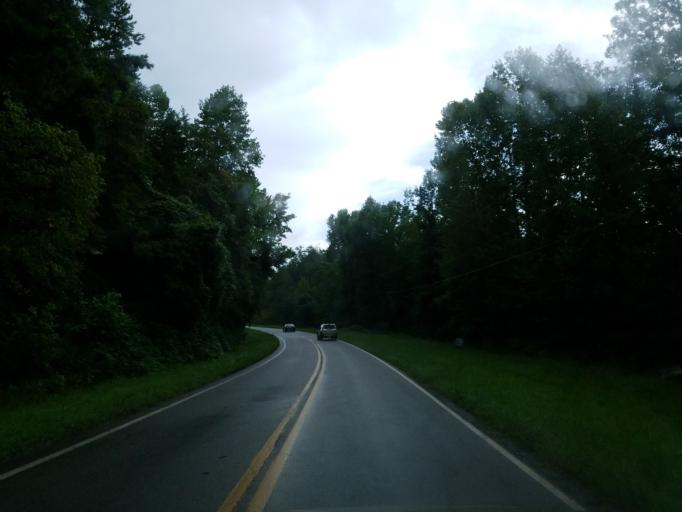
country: US
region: Georgia
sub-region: Lumpkin County
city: Dahlonega
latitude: 34.5478
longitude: -83.8846
